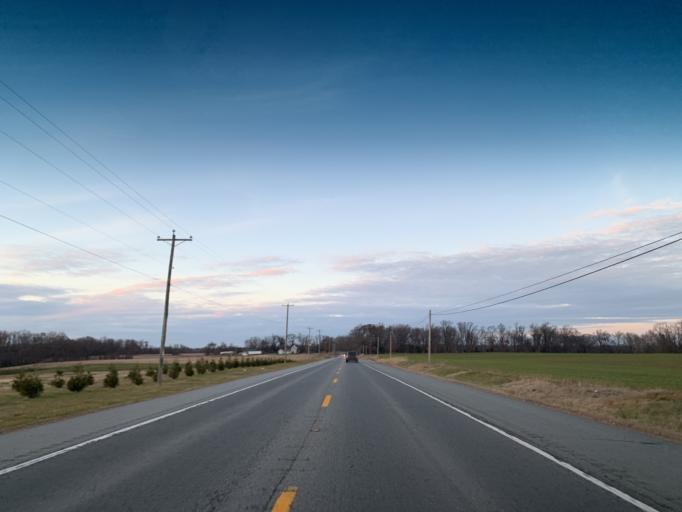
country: US
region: Delaware
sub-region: New Castle County
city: Middletown
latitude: 39.4488
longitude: -75.8693
